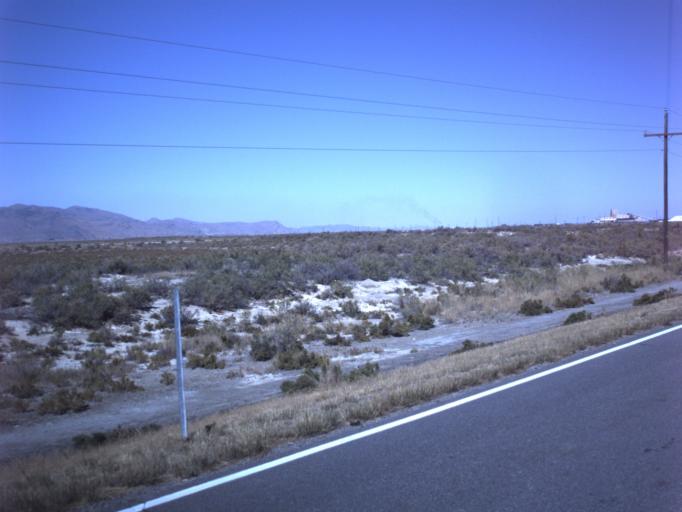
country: US
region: Utah
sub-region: Tooele County
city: Grantsville
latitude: 40.7344
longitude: -112.6564
